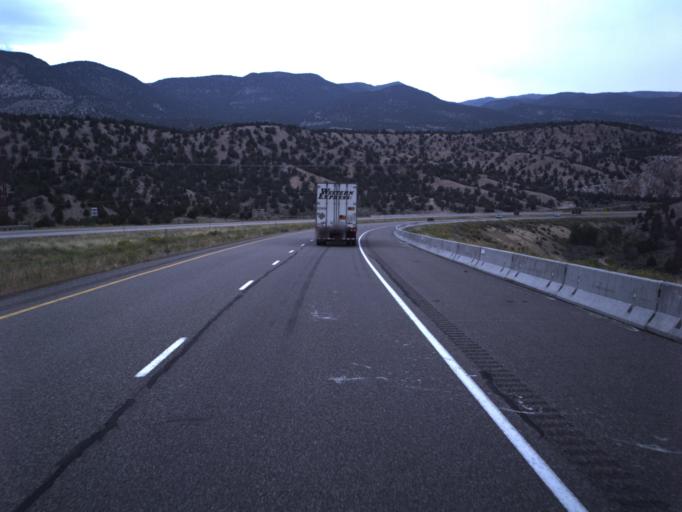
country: US
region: Utah
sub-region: Sevier County
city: Monroe
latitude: 38.5575
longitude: -112.3625
